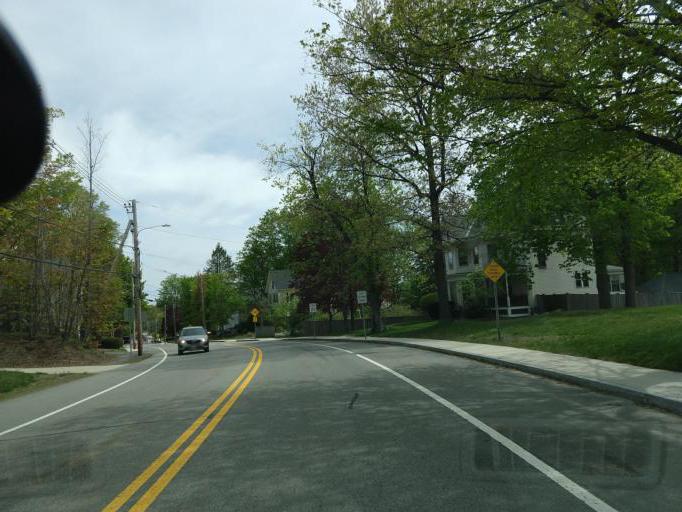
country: US
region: Massachusetts
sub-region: Essex County
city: Merrimac
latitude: 42.8287
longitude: -71.0086
